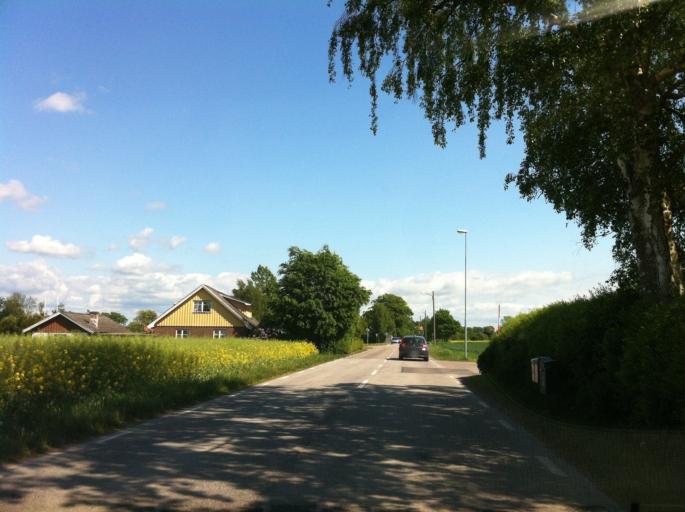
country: SE
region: Skane
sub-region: Helsingborg
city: Glumslov
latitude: 55.9670
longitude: 12.8294
